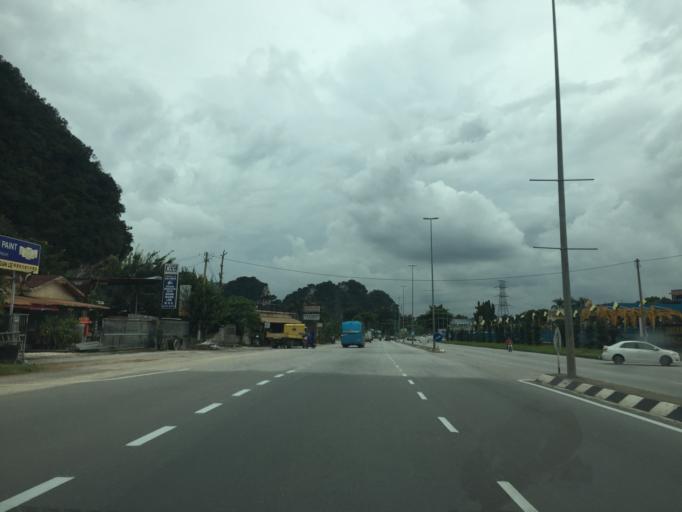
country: MY
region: Perak
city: Ipoh
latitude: 4.5547
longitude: 101.1155
